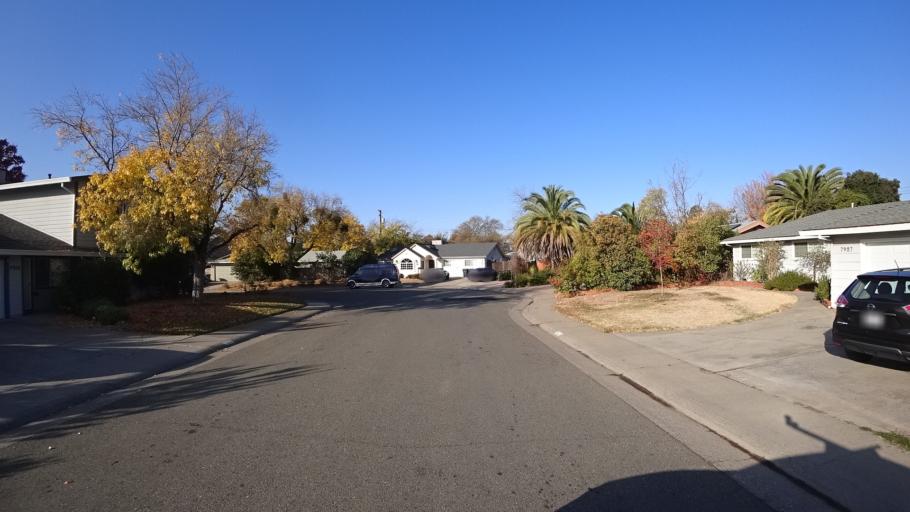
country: US
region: California
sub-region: Sacramento County
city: Citrus Heights
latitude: 38.6996
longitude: -121.2681
